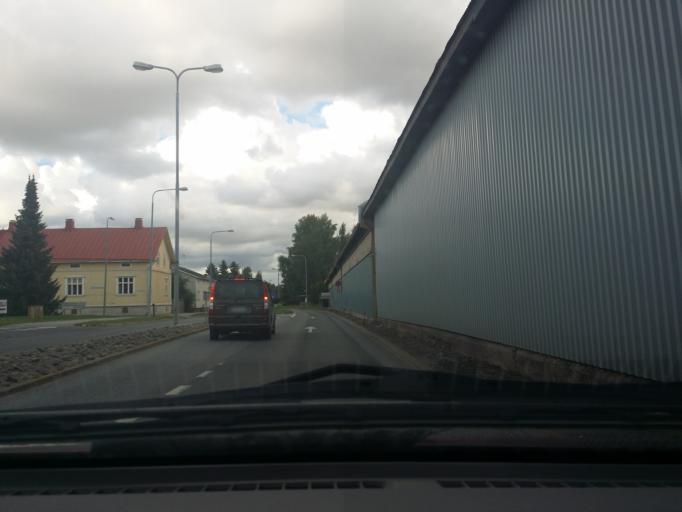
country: FI
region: Satakunta
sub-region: Pori
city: Pori
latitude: 61.4951
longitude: 21.8047
